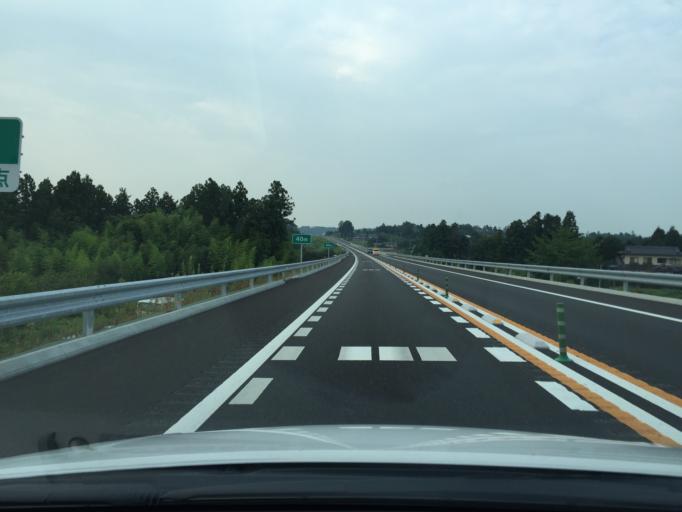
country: JP
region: Fukushima
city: Namie
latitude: 37.5573
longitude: 140.9453
